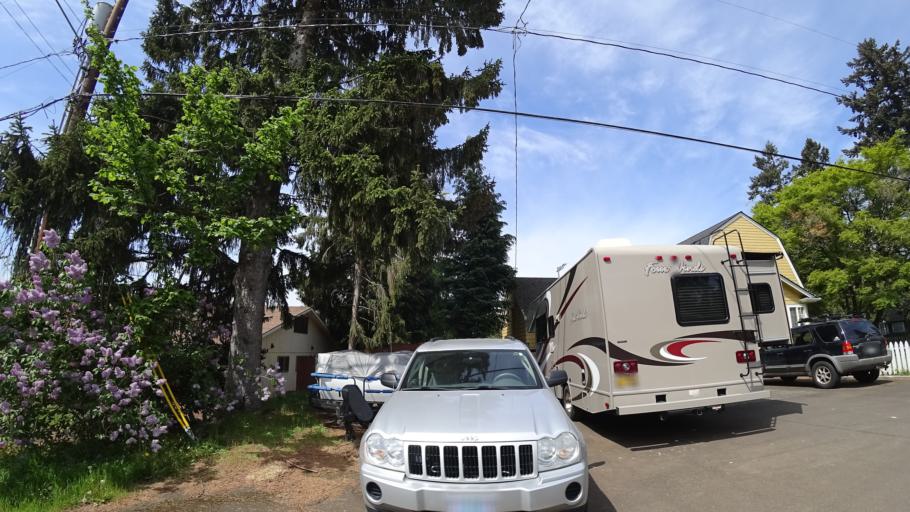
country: US
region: Oregon
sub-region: Clackamas County
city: Milwaukie
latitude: 45.4476
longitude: -122.6118
